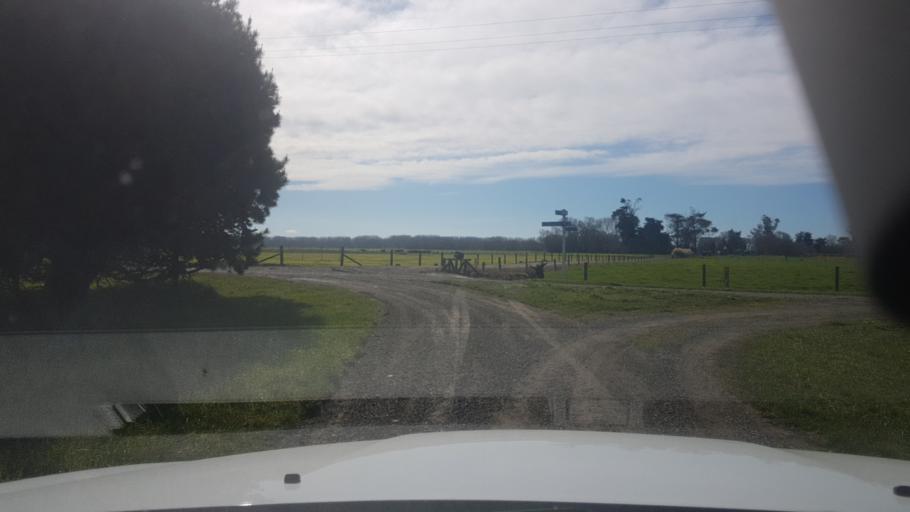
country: NZ
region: Canterbury
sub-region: Timaru District
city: Timaru
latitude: -44.2480
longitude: 171.3815
